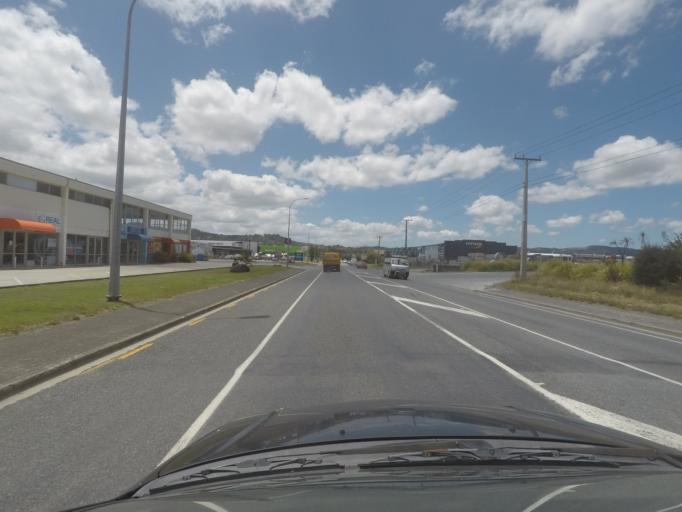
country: NZ
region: Northland
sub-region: Whangarei
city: Whangarei
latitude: -35.7424
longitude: 174.3315
